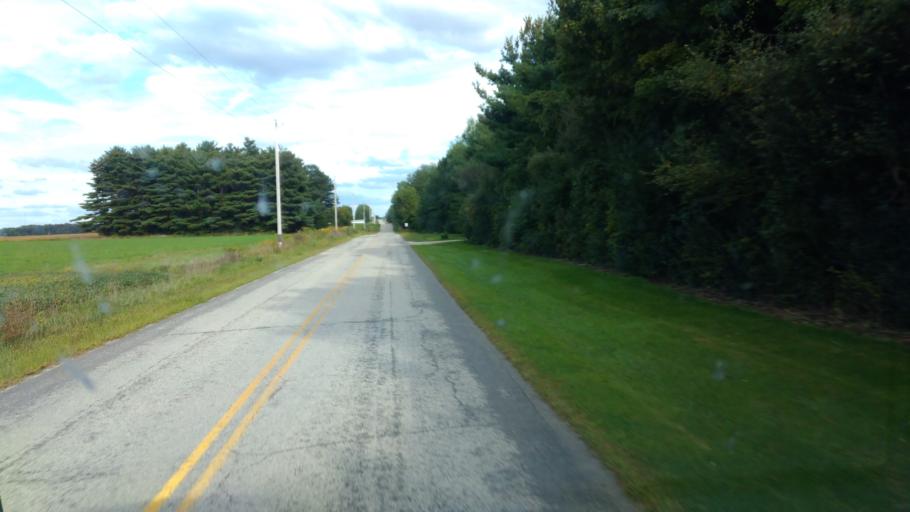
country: US
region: Ohio
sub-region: Crawford County
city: Bucyrus
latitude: 40.9212
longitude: -82.9924
